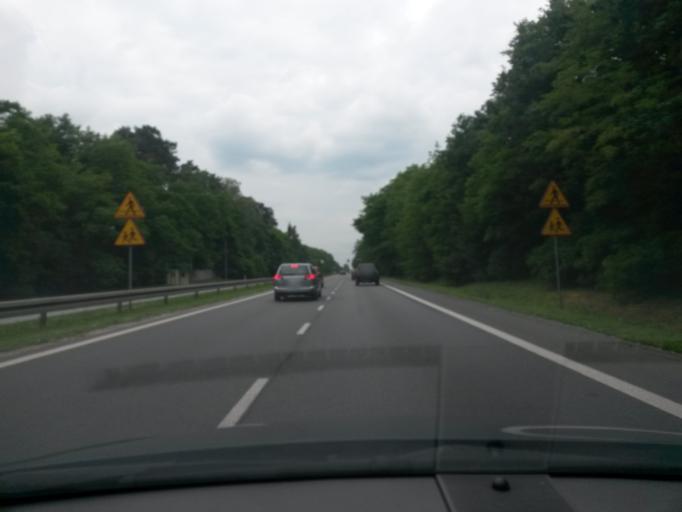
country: PL
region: Lodz Voivodeship
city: Zabia Wola
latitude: 52.0615
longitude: 20.7389
